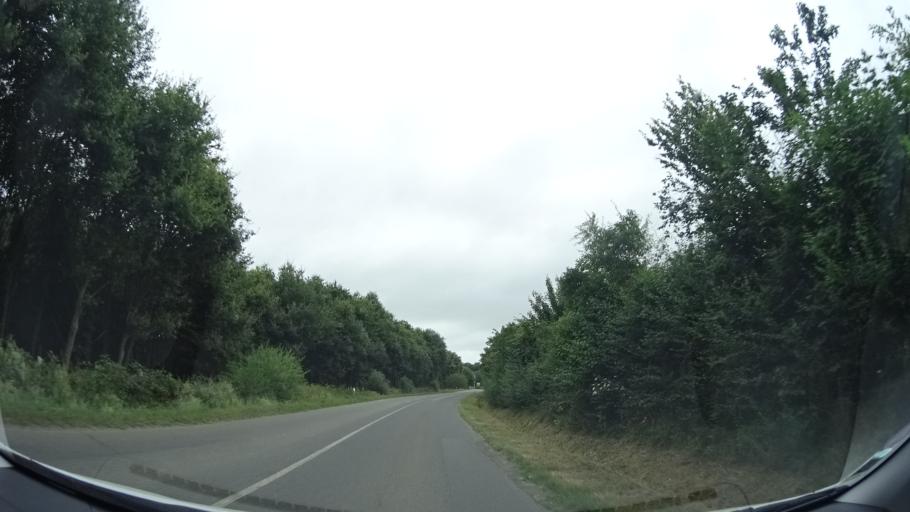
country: FR
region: Brittany
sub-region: Departement d'Ille-et-Vilaine
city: Quebriac
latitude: 48.3797
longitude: -1.8351
